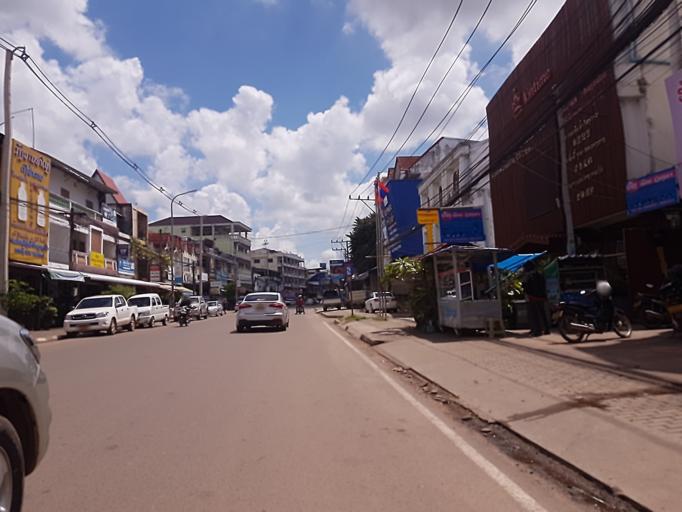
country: LA
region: Vientiane
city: Vientiane
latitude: 17.9633
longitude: 102.6210
